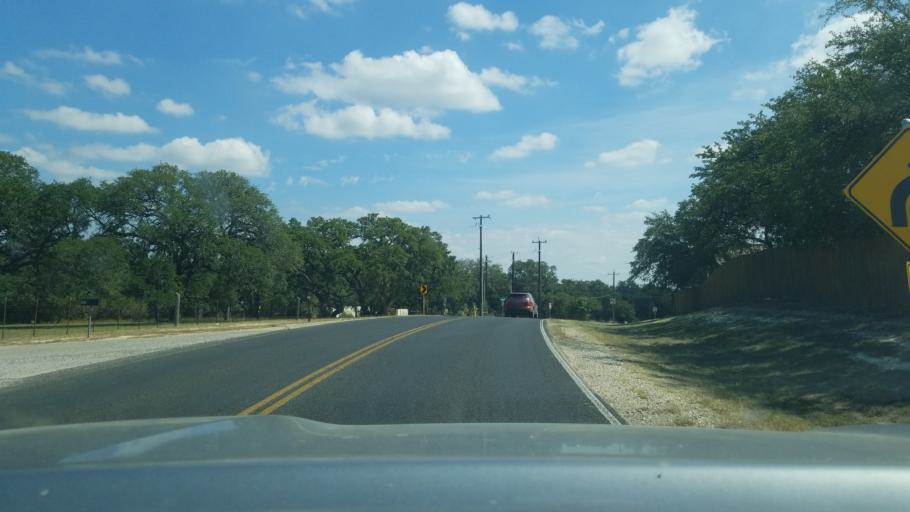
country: US
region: Texas
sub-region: Bexar County
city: Scenic Oaks
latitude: 29.7317
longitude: -98.6667
